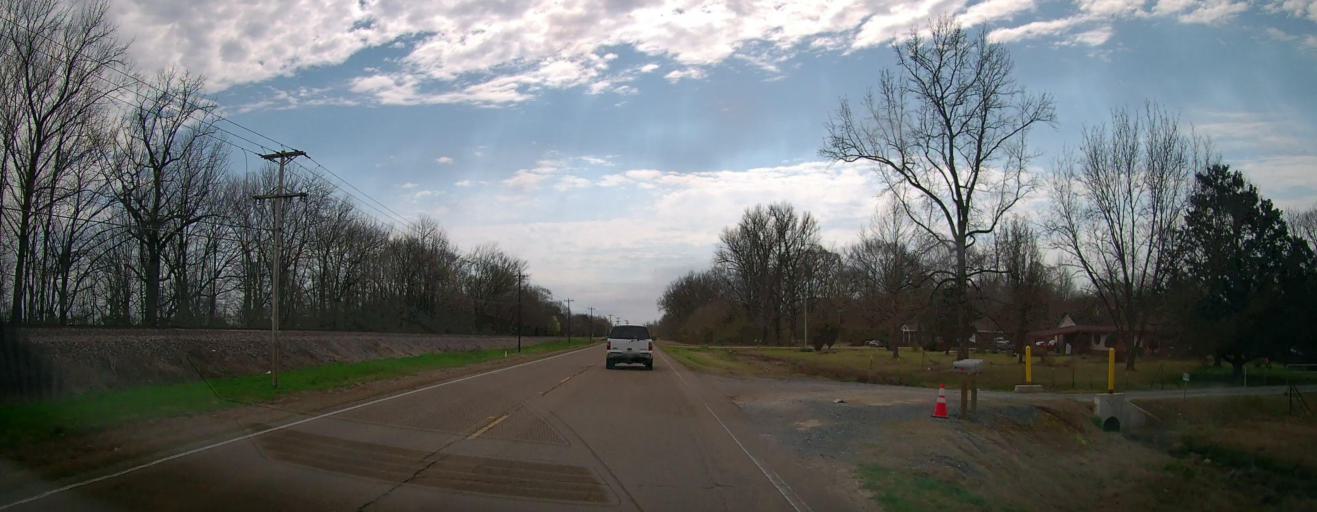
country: US
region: Mississippi
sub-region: De Soto County
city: Olive Branch
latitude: 34.9203
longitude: -89.7714
